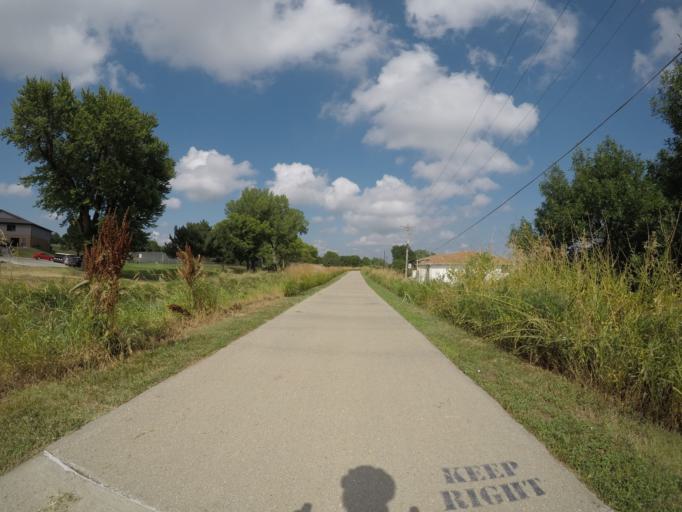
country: US
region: Nebraska
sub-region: Buffalo County
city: Kearney
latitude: 40.7030
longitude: -99.1053
